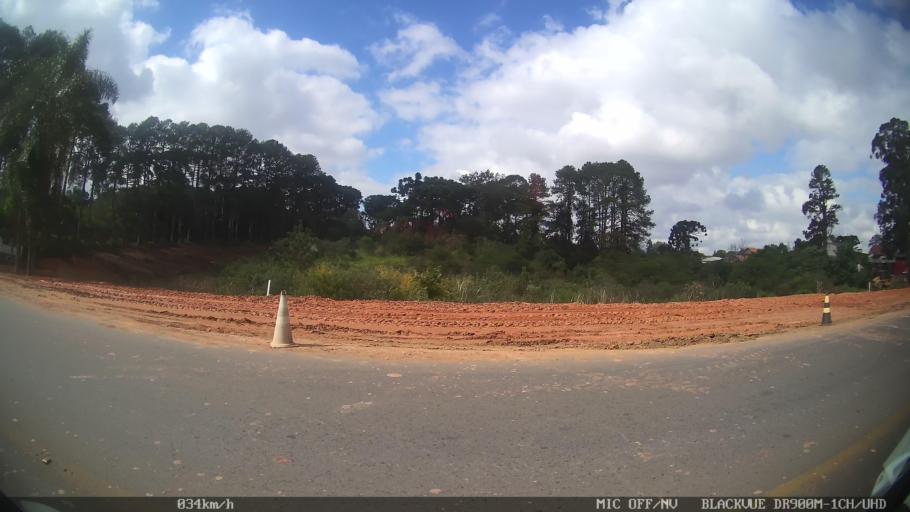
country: BR
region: Parana
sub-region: Colombo
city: Colombo
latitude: -25.3668
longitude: -49.2160
